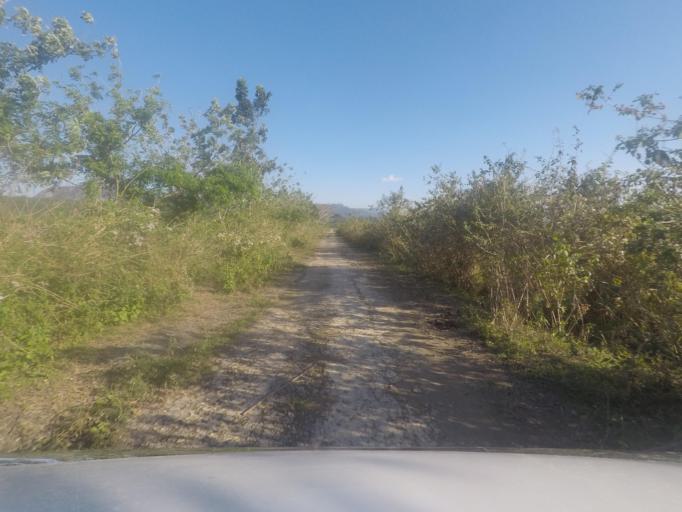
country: TL
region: Lautem
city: Lospalos
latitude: -8.4063
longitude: 127.1983
